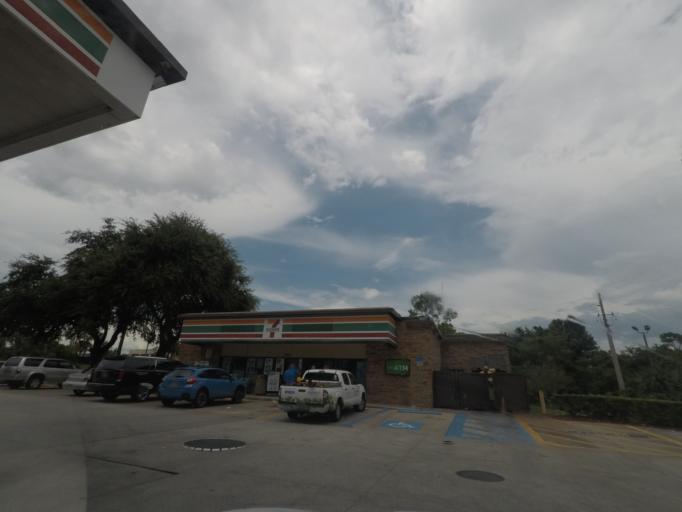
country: US
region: Florida
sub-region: Osceola County
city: Celebration
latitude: 28.3330
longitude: -81.5832
